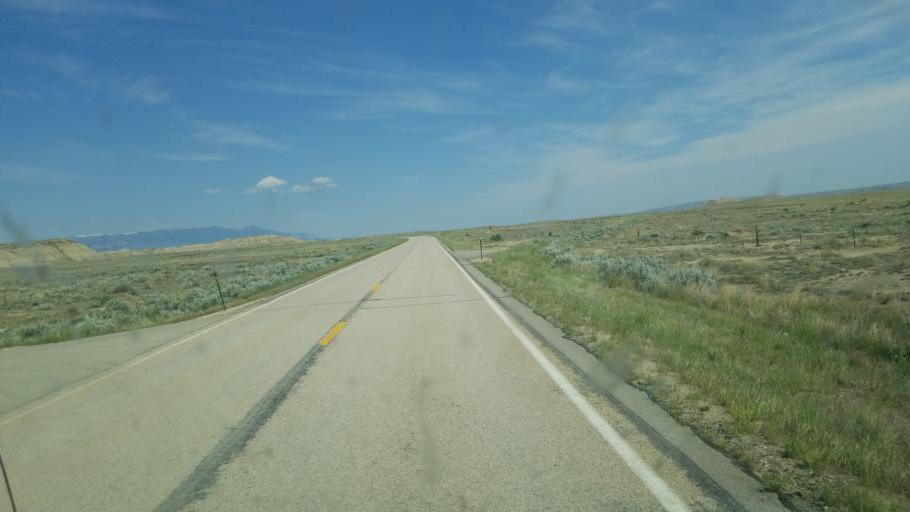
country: US
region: Wyoming
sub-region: Park County
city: Powell
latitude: 44.8284
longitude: -108.9780
